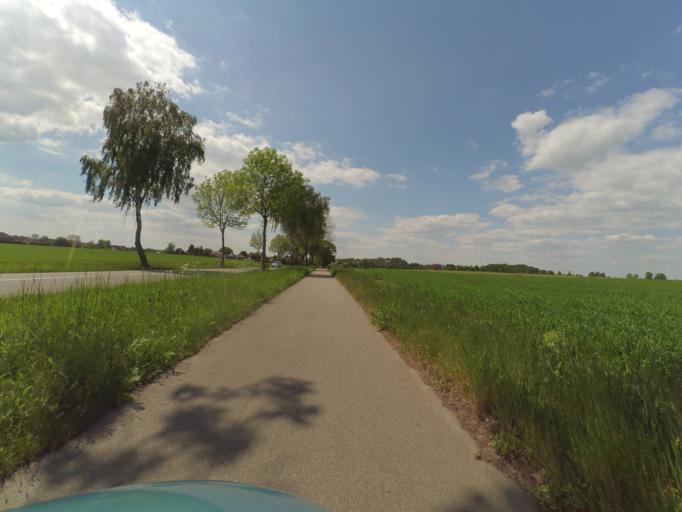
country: DE
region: Lower Saxony
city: Ummern
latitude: 52.5913
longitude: 10.4502
